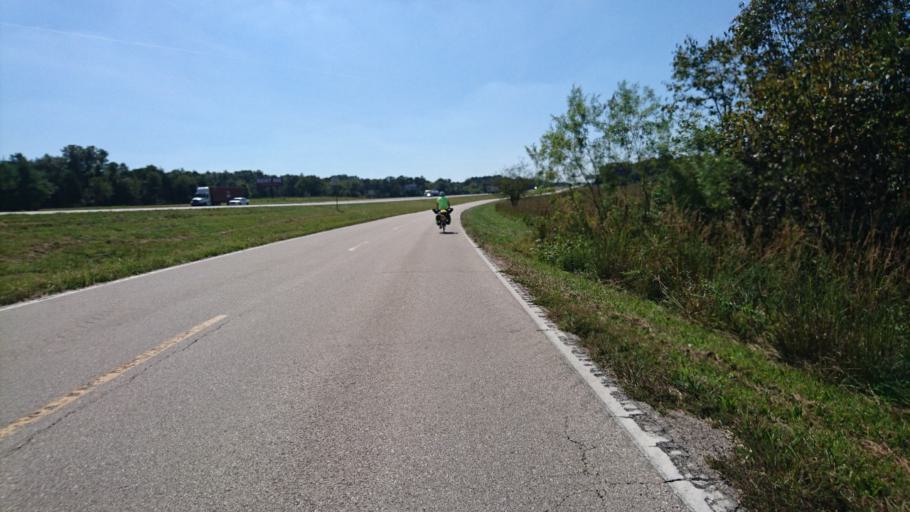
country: US
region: Missouri
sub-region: Franklin County
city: Sullivan
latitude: 38.2674
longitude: -91.1108
